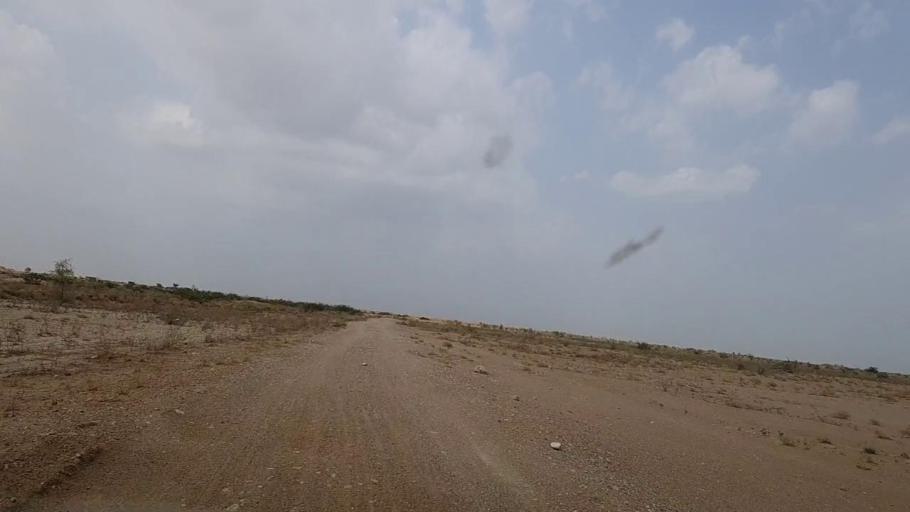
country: PK
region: Sindh
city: Kotri
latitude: 25.2797
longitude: 68.2255
